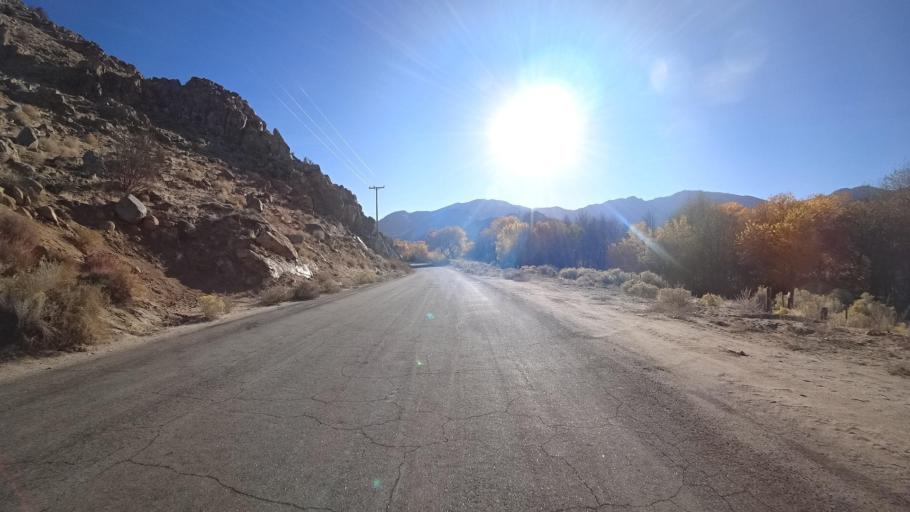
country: US
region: California
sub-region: Kern County
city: Weldon
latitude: 35.5791
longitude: -118.2501
